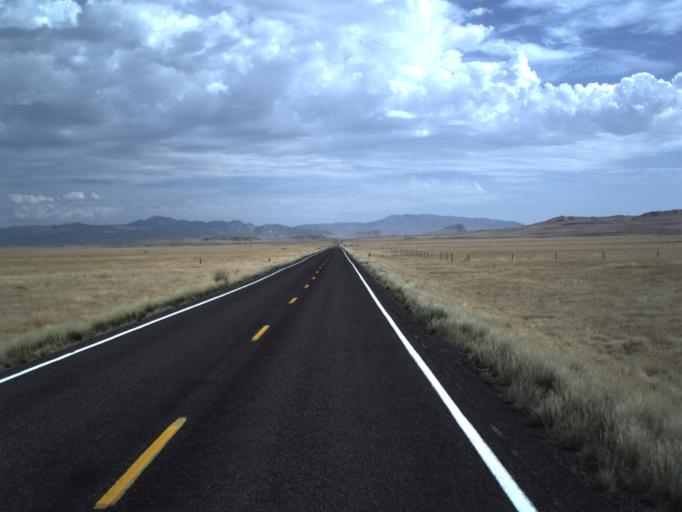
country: US
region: Utah
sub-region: Tooele County
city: Wendover
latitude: 41.3898
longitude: -113.9747
